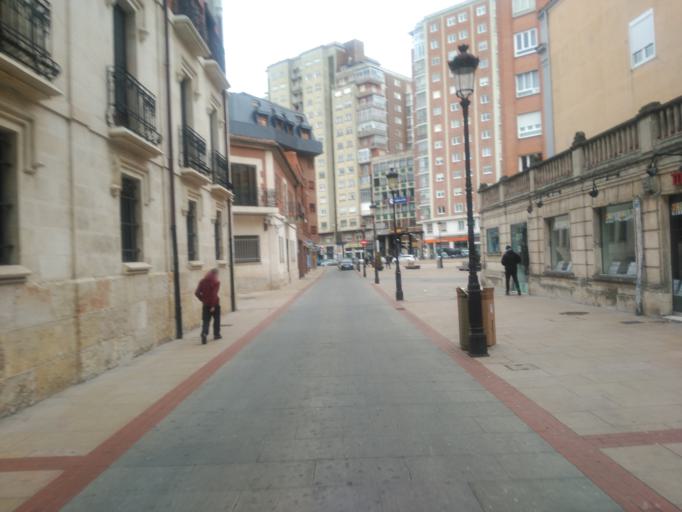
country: ES
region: Castille and Leon
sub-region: Provincia de Burgos
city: Burgos
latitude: 42.3438
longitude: -3.6999
